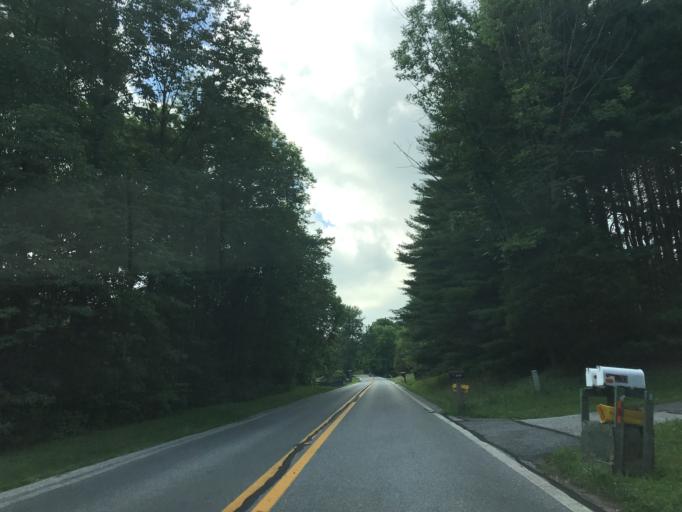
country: US
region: Maryland
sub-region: Carroll County
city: Hampstead
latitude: 39.6613
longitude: -76.8145
